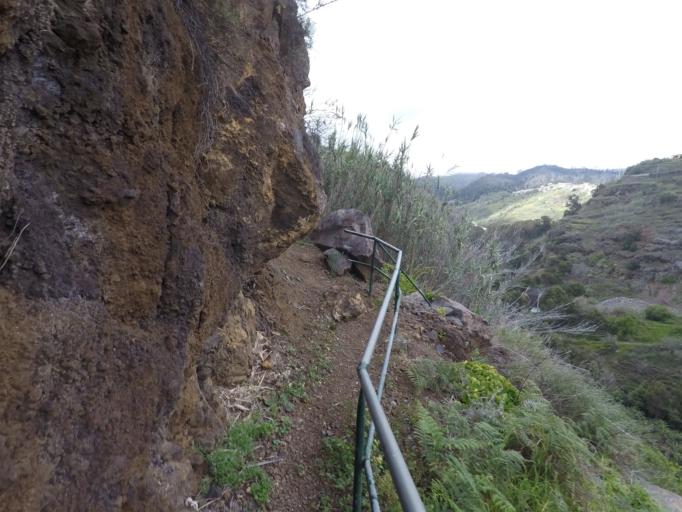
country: PT
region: Madeira
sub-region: Calheta
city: Estreito da Calheta
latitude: 32.7301
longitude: -17.1815
